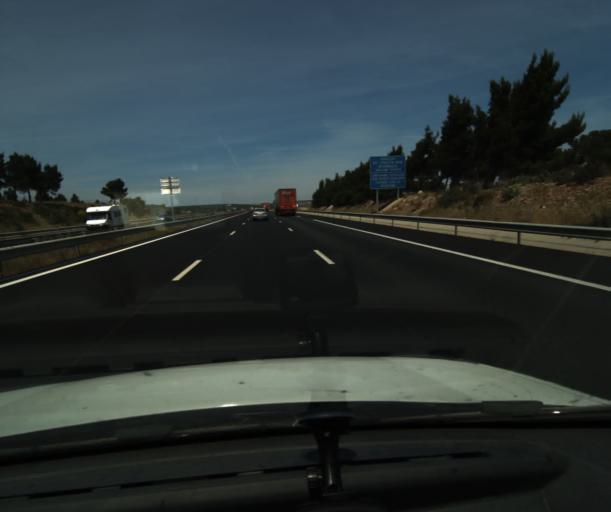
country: FR
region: Languedoc-Roussillon
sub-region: Departement de l'Aude
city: Leucate
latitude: 42.9506
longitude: 2.9710
